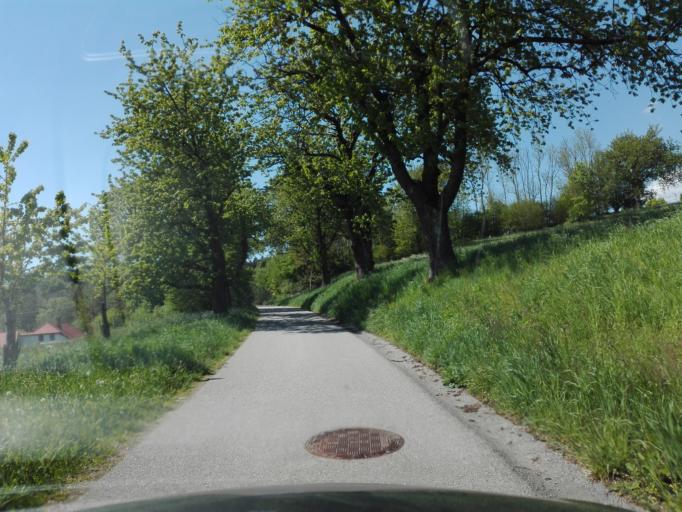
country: AT
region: Upper Austria
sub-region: Politischer Bezirk Urfahr-Umgebung
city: Feldkirchen an der Donau
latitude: 48.3437
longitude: 13.9676
